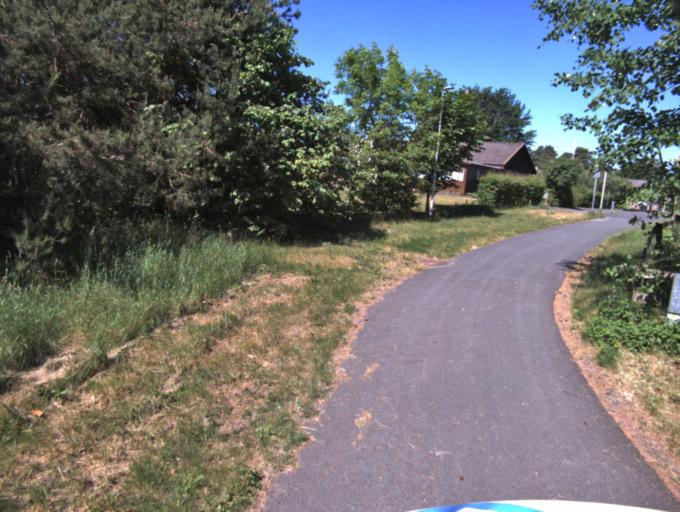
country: SE
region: Skane
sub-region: Kristianstads Kommun
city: Ahus
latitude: 55.9427
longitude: 14.2910
